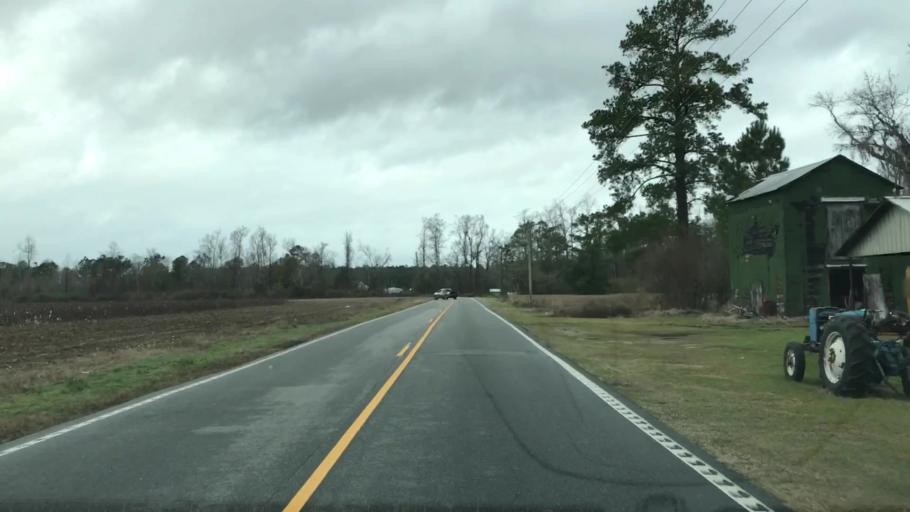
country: US
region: South Carolina
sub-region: Florence County
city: Johnsonville
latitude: 33.6528
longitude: -79.3019
